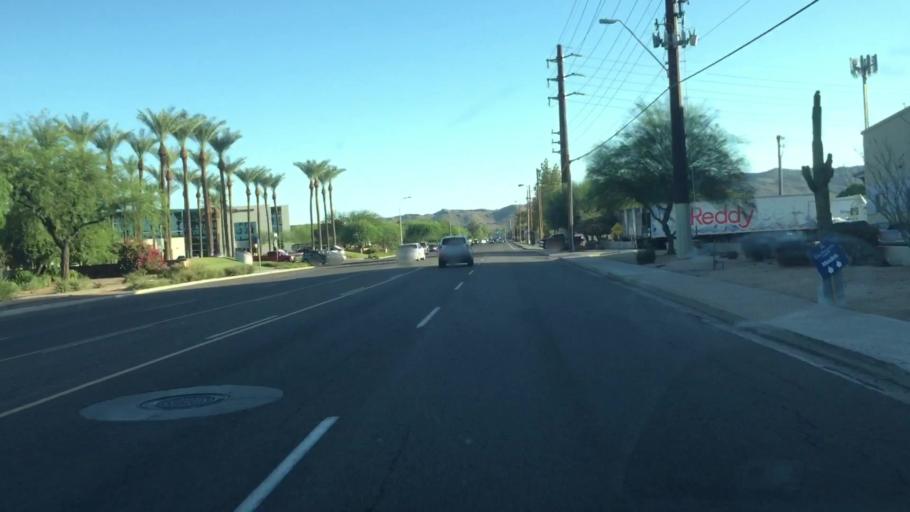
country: US
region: Arizona
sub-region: Maricopa County
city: Guadalupe
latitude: 33.4047
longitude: -111.9954
